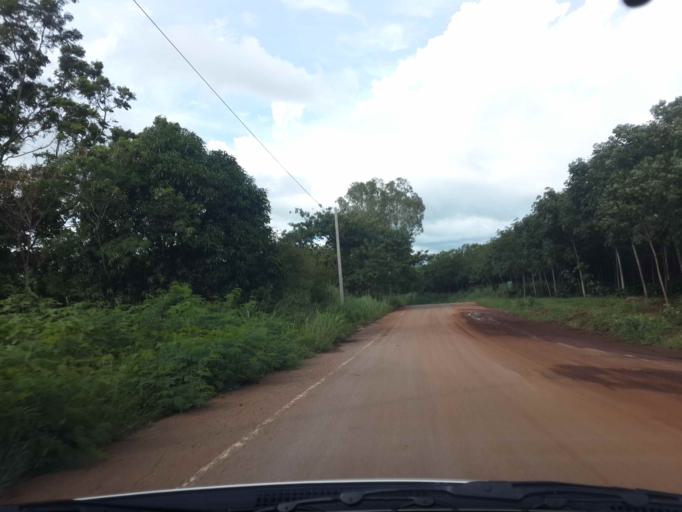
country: TH
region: Kanchanaburi
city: Dan Makham Tia
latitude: 13.7423
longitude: 99.1981
